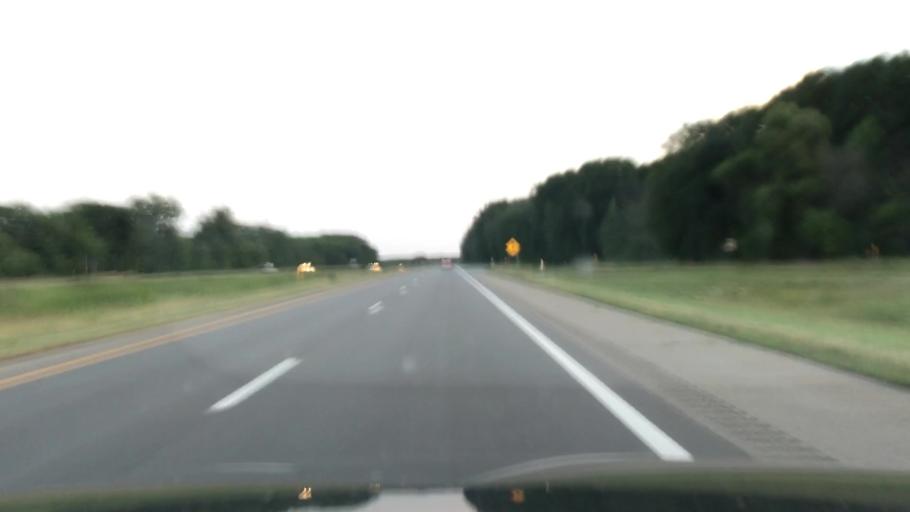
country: US
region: Michigan
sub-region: Montcalm County
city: Howard City
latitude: 43.3349
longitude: -85.5128
